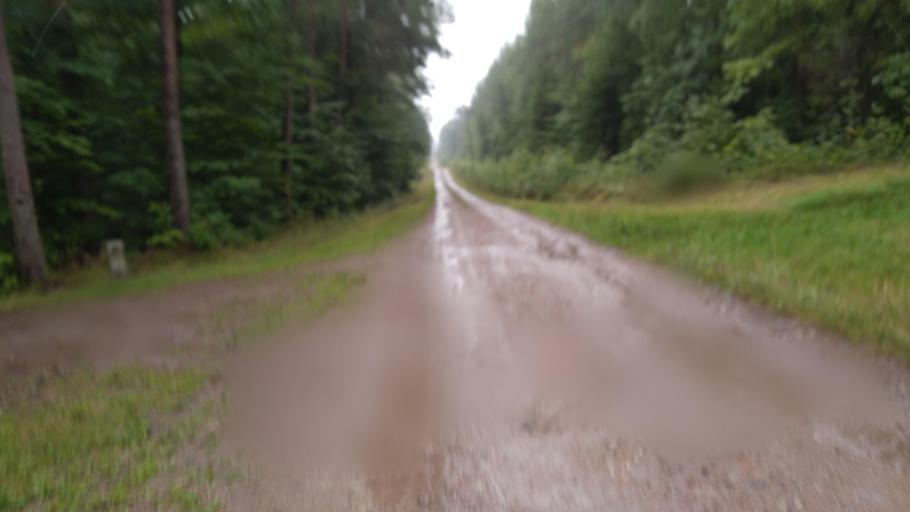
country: PL
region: Pomeranian Voivodeship
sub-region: Powiat wejherowski
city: Goscicino
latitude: 54.6237
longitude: 18.1470
